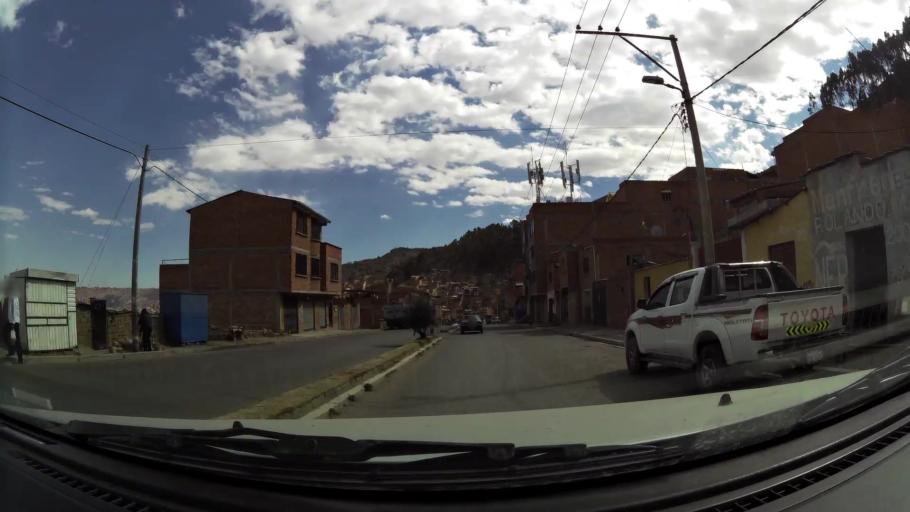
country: BO
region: La Paz
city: La Paz
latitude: -16.4652
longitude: -68.1150
